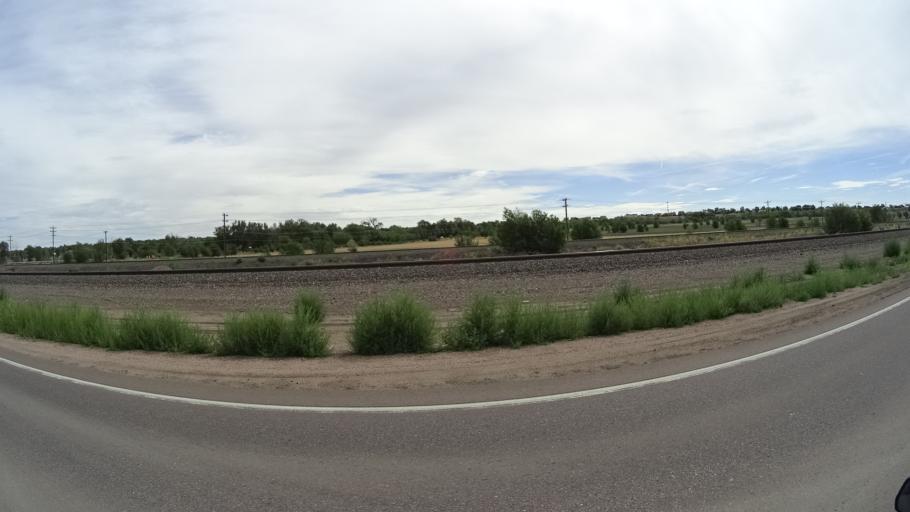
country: US
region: Colorado
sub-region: El Paso County
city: Security-Widefield
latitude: 38.7143
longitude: -104.7141
